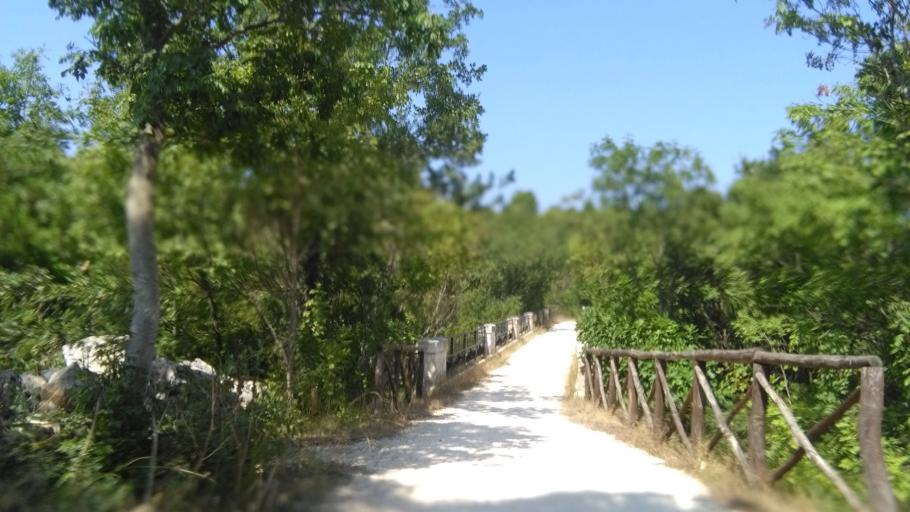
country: IT
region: Apulia
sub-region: Provincia di Brindisi
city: Cisternino
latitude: 40.6827
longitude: 17.4316
